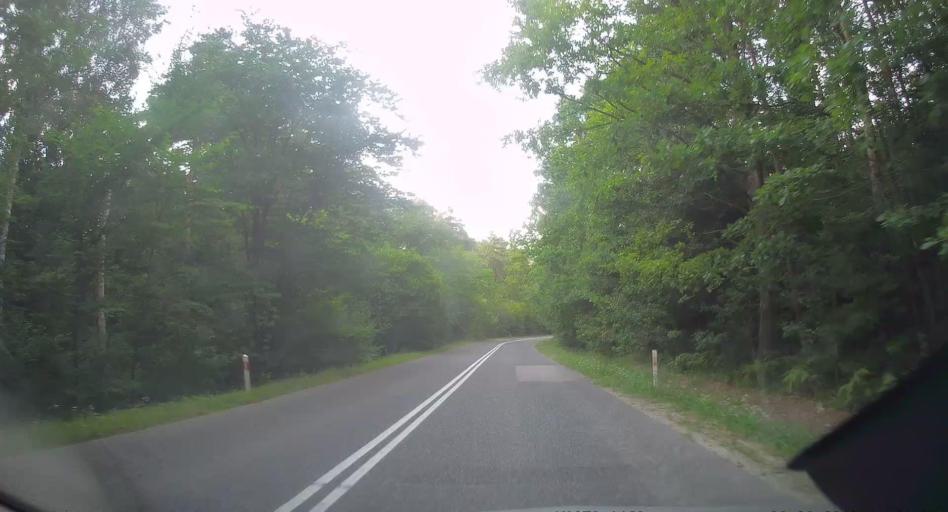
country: PL
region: Swietokrzyskie
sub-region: Powiat kielecki
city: Lopuszno
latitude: 50.8869
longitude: 20.2597
